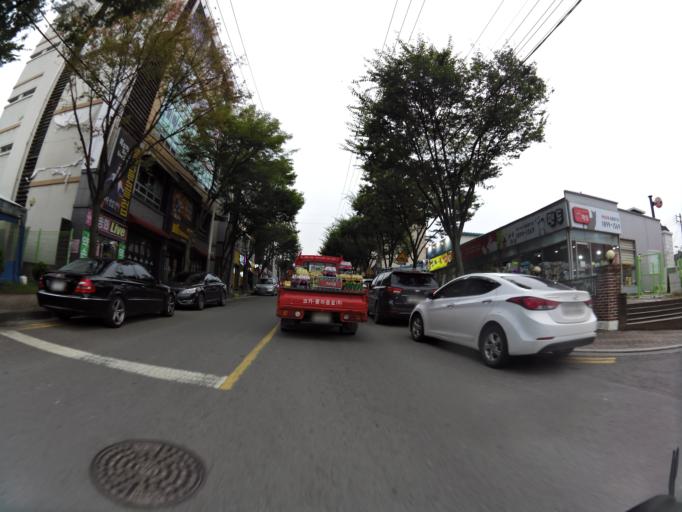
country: KR
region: Gyeongsangbuk-do
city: Gyeongsan-si
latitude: 35.8425
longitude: 128.7505
